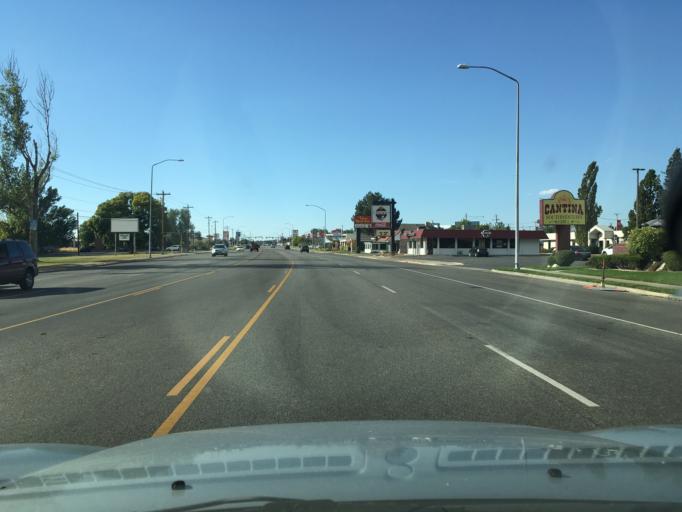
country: US
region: Utah
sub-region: Davis County
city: Layton
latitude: 41.0643
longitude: -111.9700
